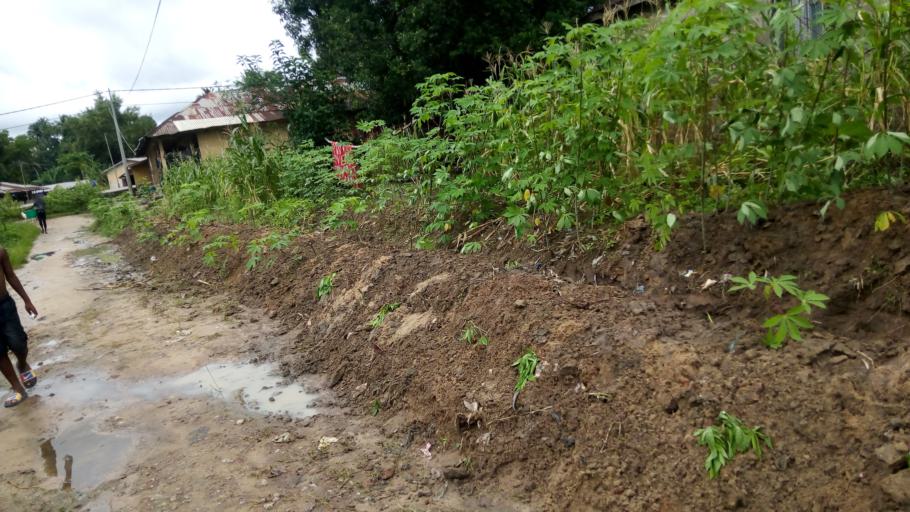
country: SL
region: Northern Province
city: Lunsar
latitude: 8.6889
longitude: -12.5353
